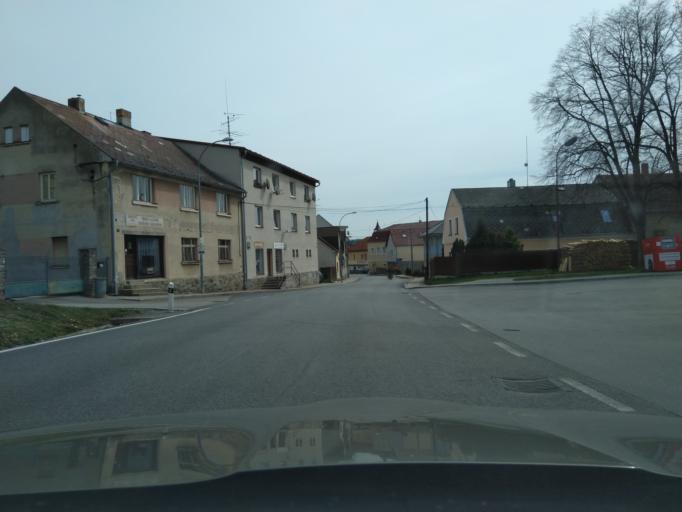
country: CZ
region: Jihocesky
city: Ckyne
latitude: 49.1153
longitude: 13.8255
